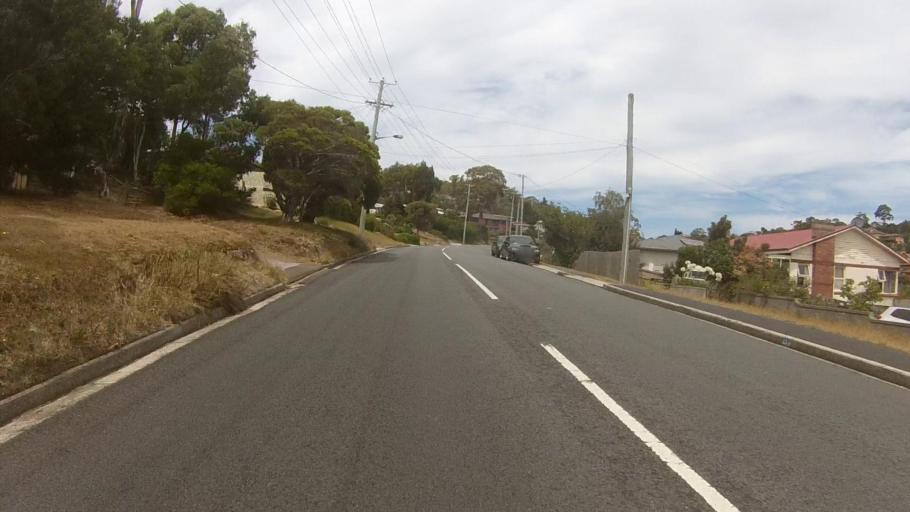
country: AU
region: Tasmania
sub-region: Clarence
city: Lindisfarne
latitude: -42.8513
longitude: 147.3691
